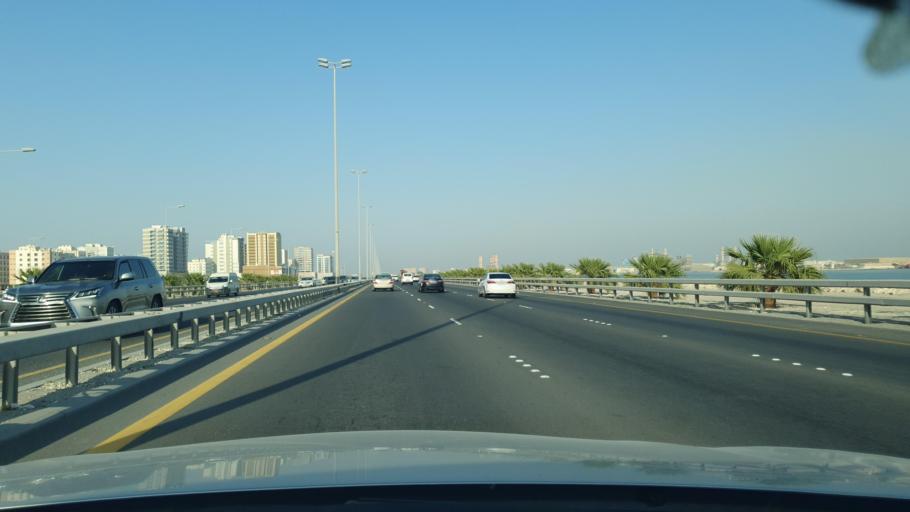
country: BH
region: Muharraq
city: Al Hadd
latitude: 26.2251
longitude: 50.6400
